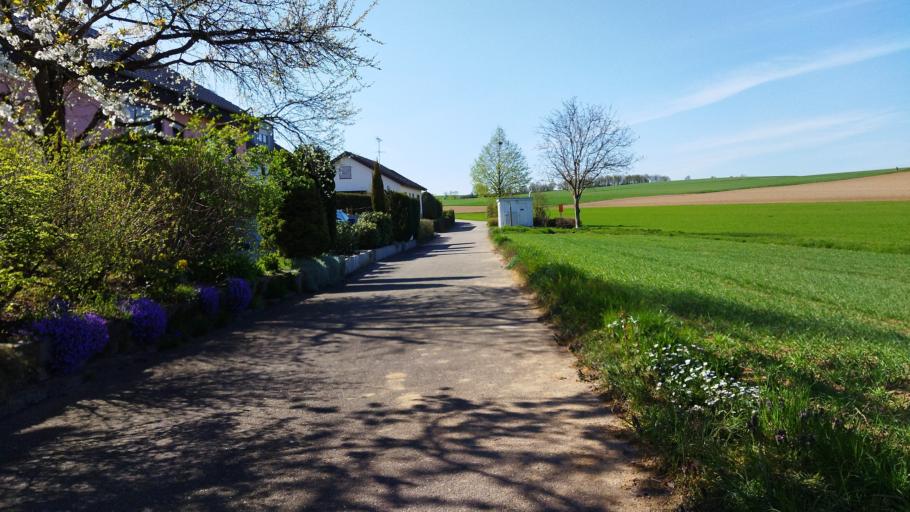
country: DE
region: Baden-Wuerttemberg
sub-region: Regierungsbezirk Stuttgart
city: Bad Wimpfen
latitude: 49.1999
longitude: 9.1554
